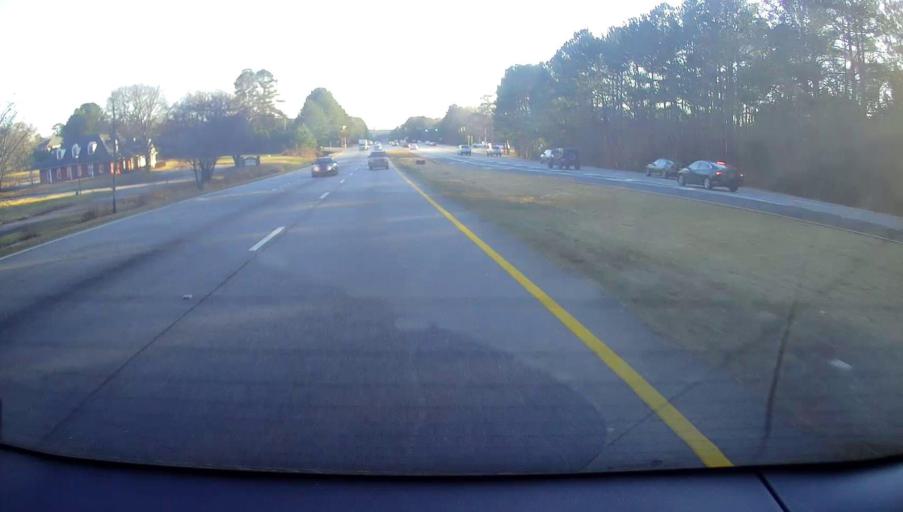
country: US
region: Georgia
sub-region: Fayette County
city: Tyrone
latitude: 33.4805
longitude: -84.5856
